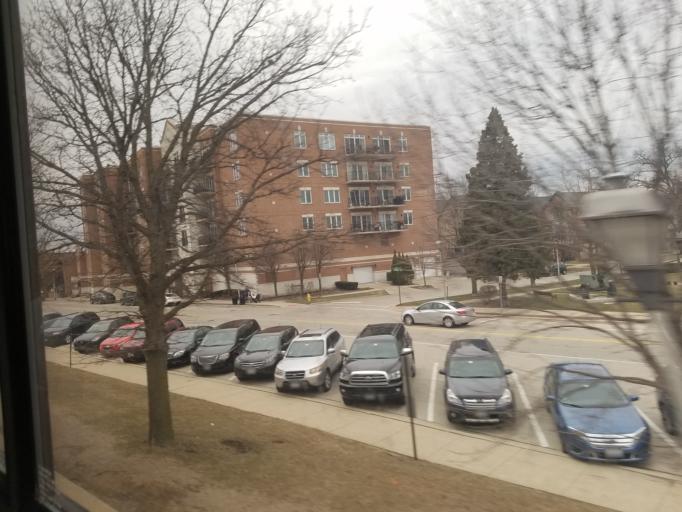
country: US
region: Illinois
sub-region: Cook County
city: Brookfield
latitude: 41.8223
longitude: -87.8423
